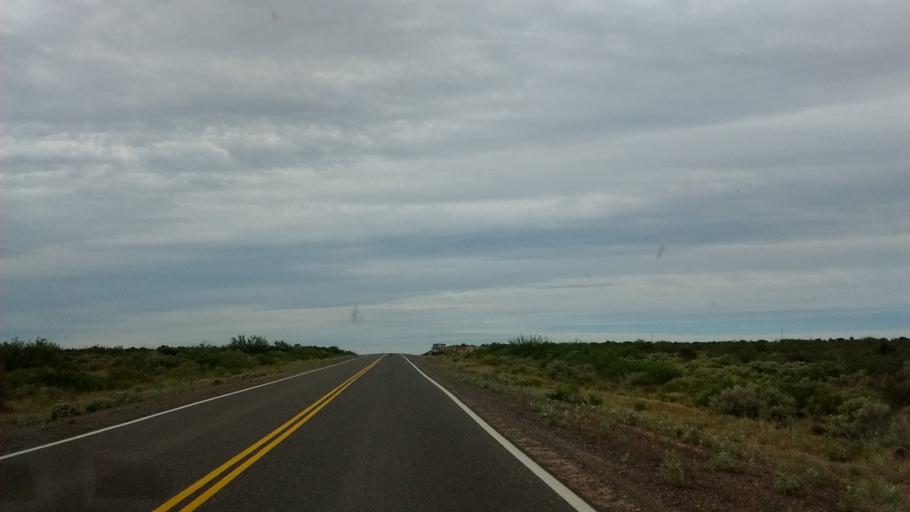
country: AR
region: Rio Negro
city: Catriel
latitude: -38.0613
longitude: -67.9215
